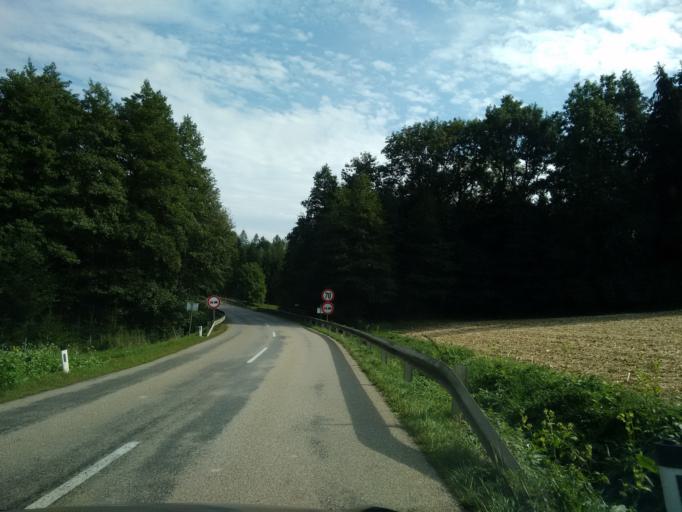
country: AT
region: Upper Austria
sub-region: Wels-Land
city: Thalheim bei Wels
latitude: 48.1303
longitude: 14.0732
